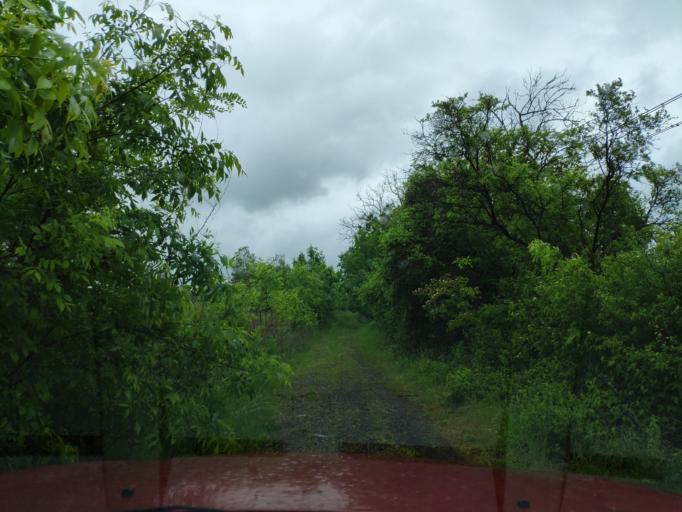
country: SK
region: Kosicky
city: Cierna nad Tisou
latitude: 48.4287
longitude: 22.0950
